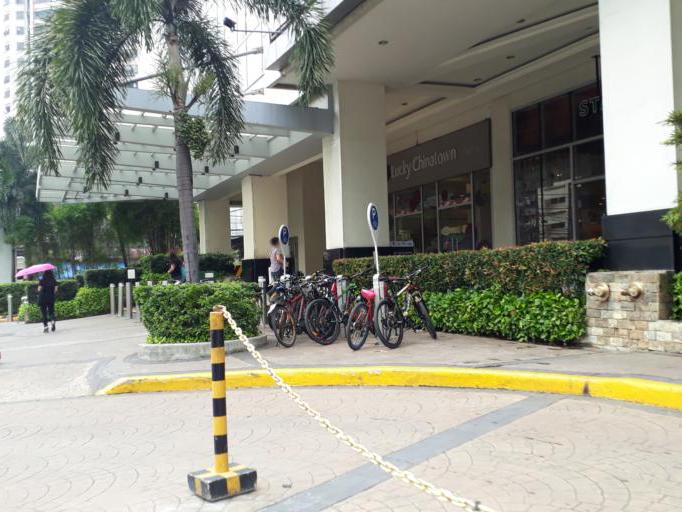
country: PH
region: Metro Manila
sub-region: City of Manila
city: Manila
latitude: 14.6029
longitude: 120.9741
